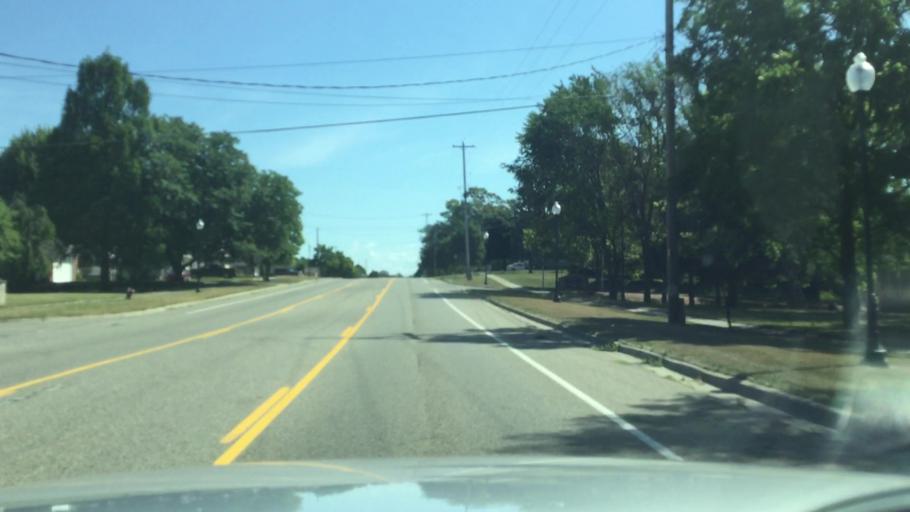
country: US
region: Michigan
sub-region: Genesee County
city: Grand Blanc
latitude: 42.9206
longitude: -83.6409
